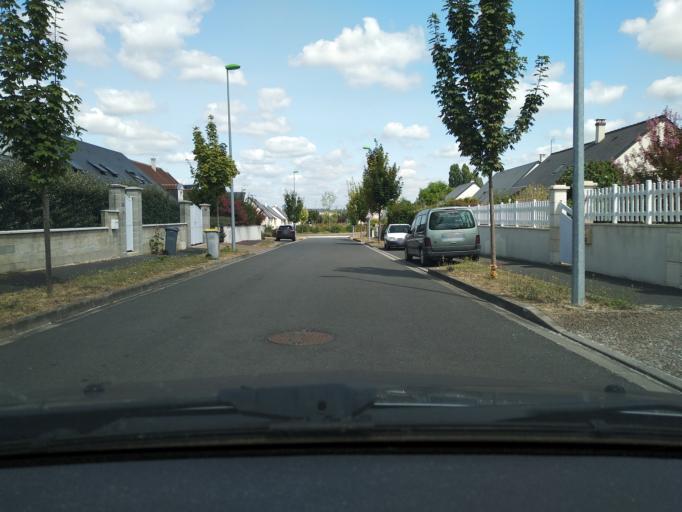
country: FR
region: Centre
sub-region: Departement d'Indre-et-Loire
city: Chanceaux-sur-Choisille
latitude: 47.4545
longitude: 0.7020
